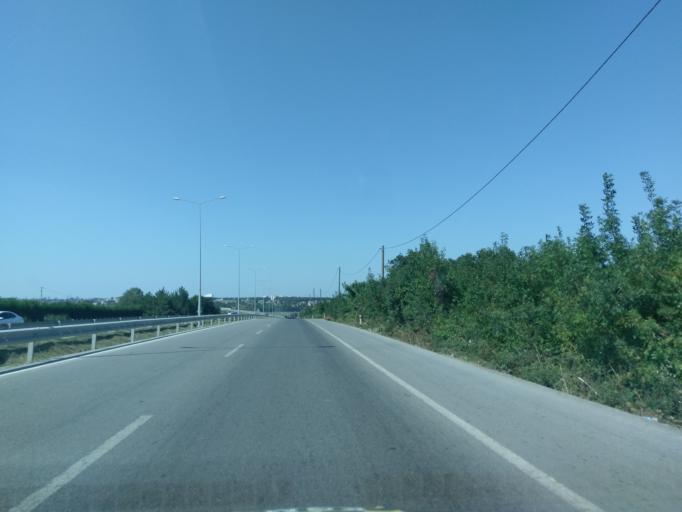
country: TR
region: Samsun
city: Bafra
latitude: 41.5310
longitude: 35.9514
